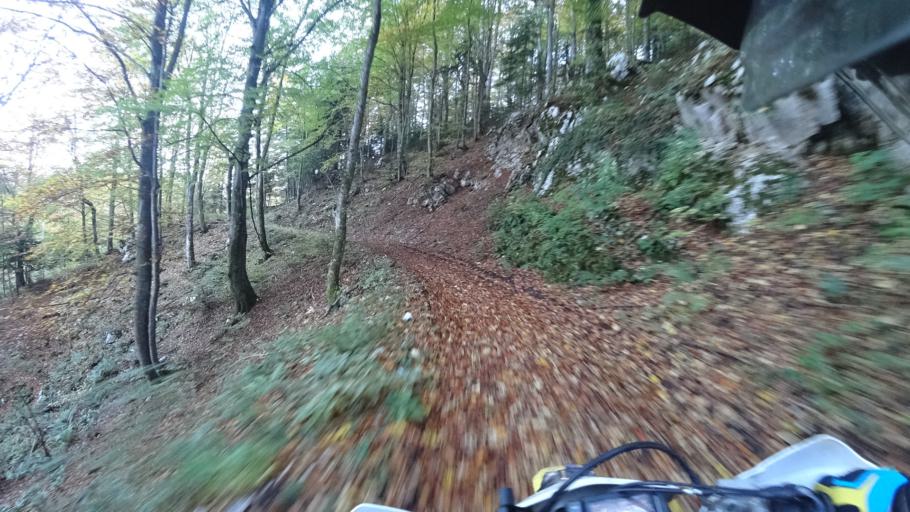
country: HR
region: Karlovacka
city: Plaski
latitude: 44.9650
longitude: 15.4387
